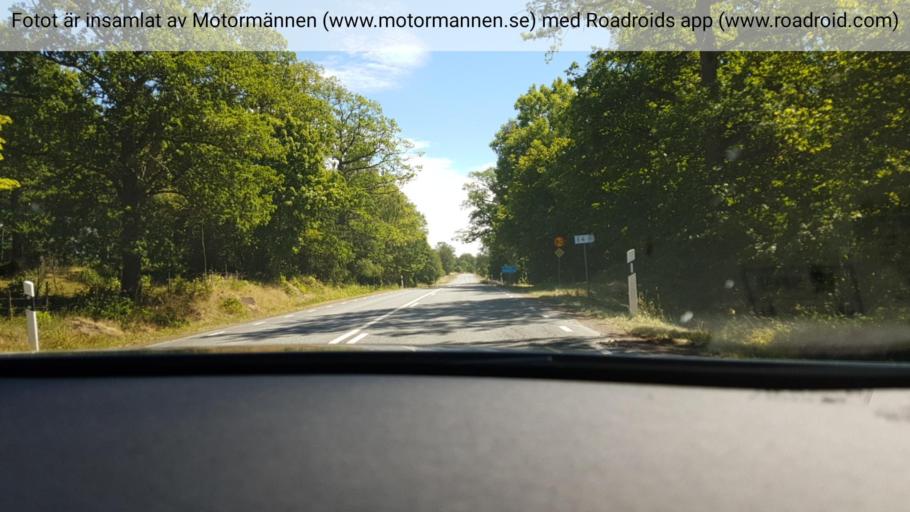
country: SE
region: Joenkoeping
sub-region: Jonkopings Kommun
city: Asa
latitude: 58.0056
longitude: 14.5948
